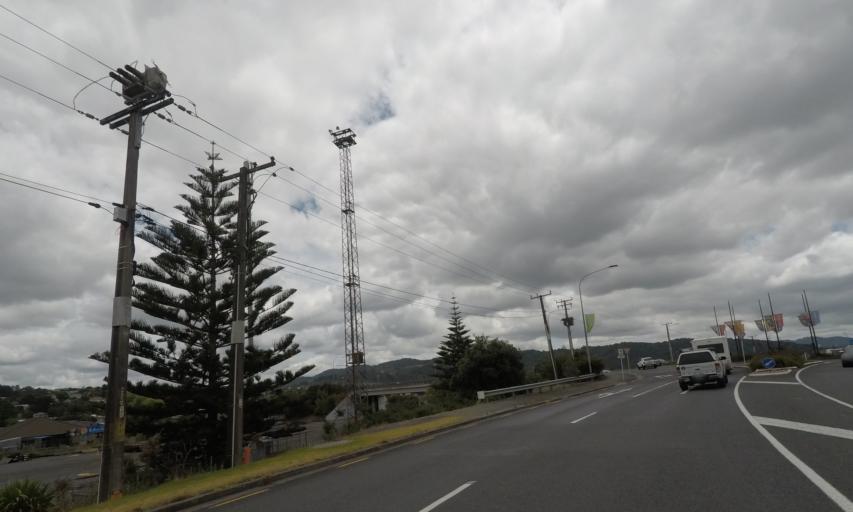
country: NZ
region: Northland
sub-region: Whangarei
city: Whangarei
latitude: -35.7340
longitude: 174.3278
